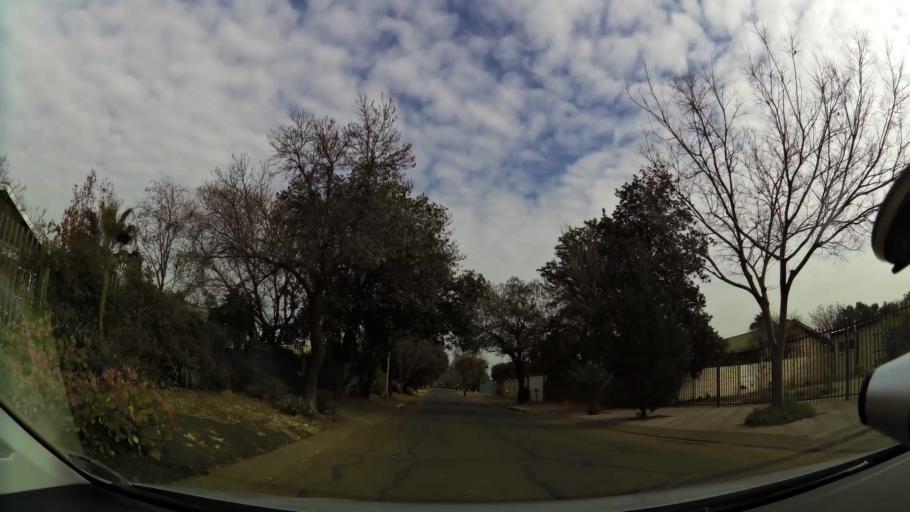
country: ZA
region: Orange Free State
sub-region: Mangaung Metropolitan Municipality
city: Bloemfontein
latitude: -29.1324
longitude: 26.1963
